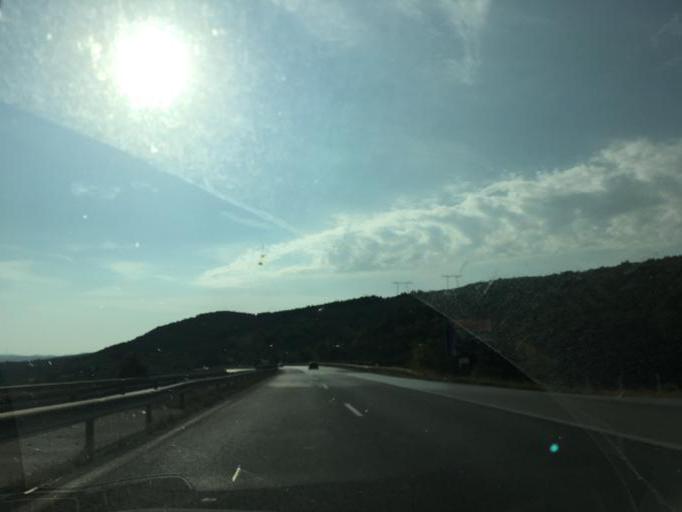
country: BG
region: Sofiya
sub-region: Obshtina Elin Pelin
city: Elin Pelin
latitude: 42.5957
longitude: 23.5895
